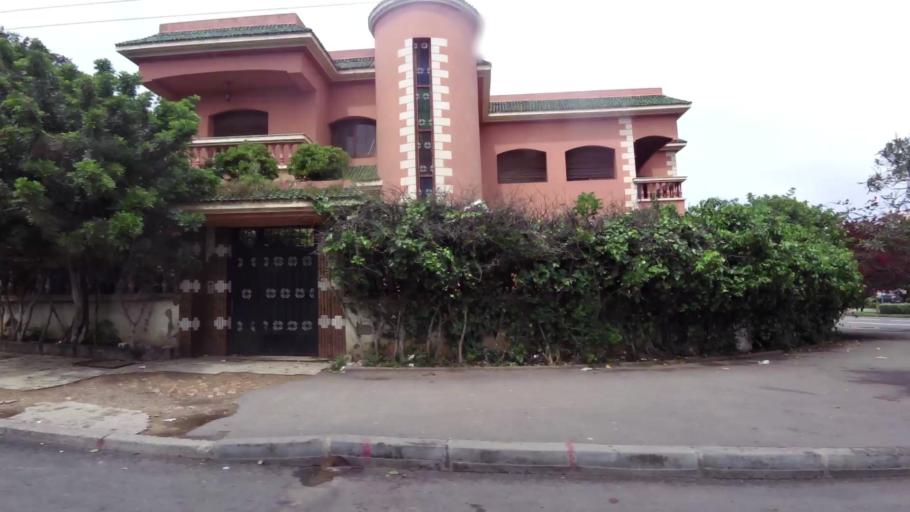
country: MA
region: Grand Casablanca
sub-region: Casablanca
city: Casablanca
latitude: 33.5539
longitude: -7.6812
